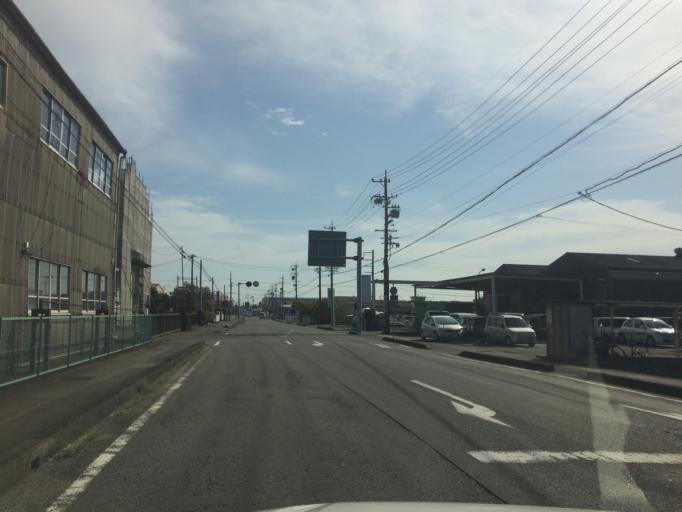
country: JP
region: Shizuoka
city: Fujieda
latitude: 34.7894
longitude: 138.2873
